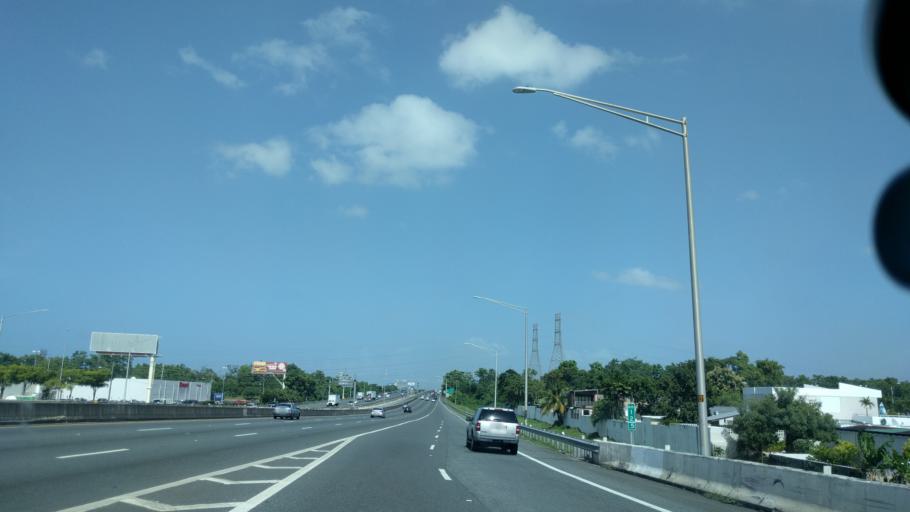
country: PR
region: Bayamon
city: Bayamon
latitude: 18.4208
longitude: -66.1622
